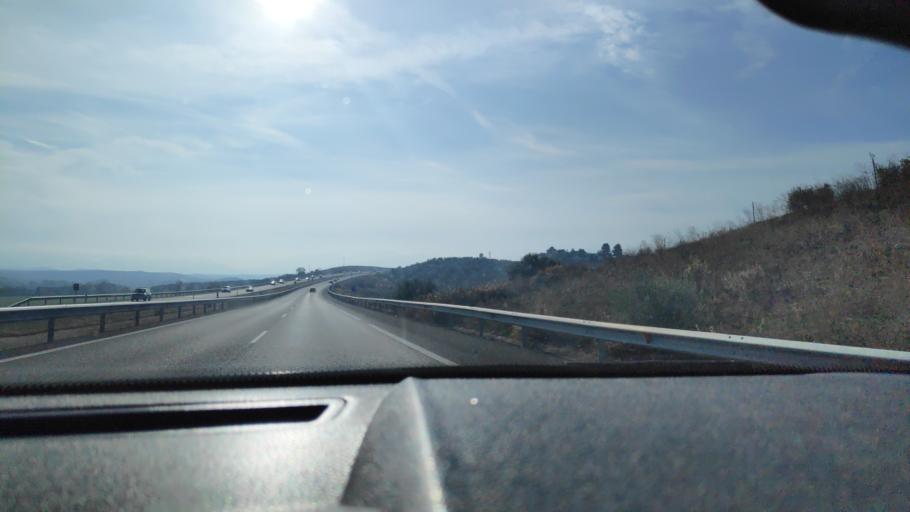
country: ES
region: Andalusia
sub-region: Provincia de Jaen
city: Jaen
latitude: 37.8703
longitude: -3.7659
